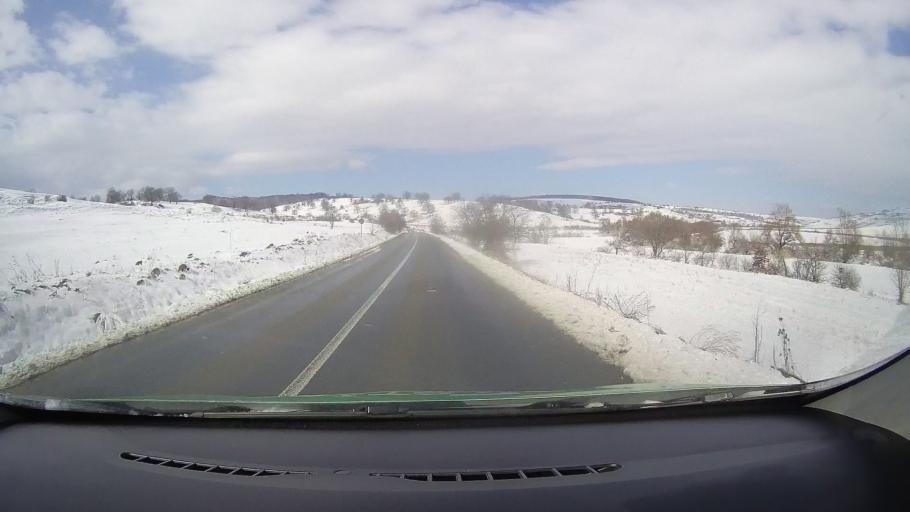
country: RO
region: Sibiu
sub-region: Comuna Altina
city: Altina
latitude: 45.9424
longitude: 24.4537
